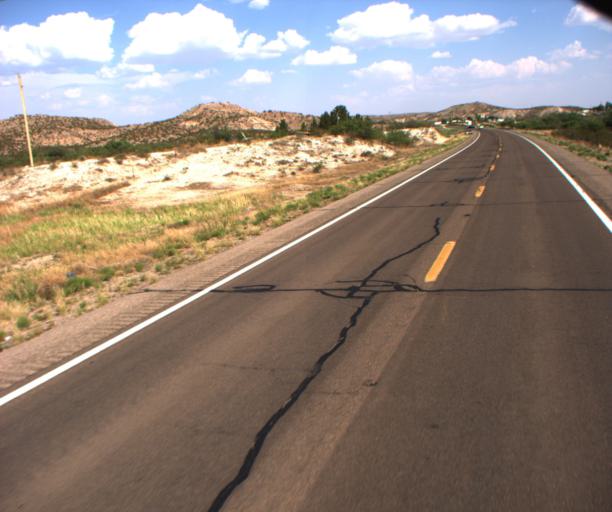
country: US
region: Arizona
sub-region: Greenlee County
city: Clifton
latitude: 32.7717
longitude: -109.1530
